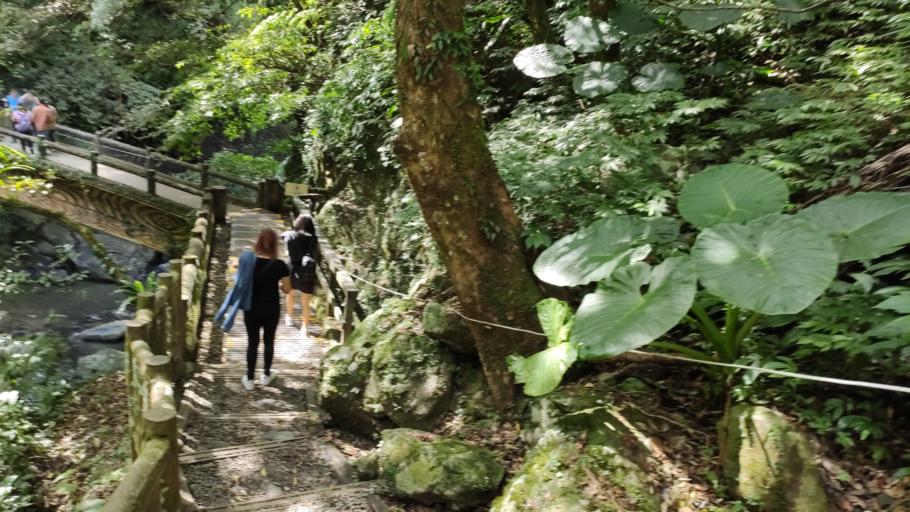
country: TW
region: Taiwan
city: Daxi
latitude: 24.8180
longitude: 121.4500
